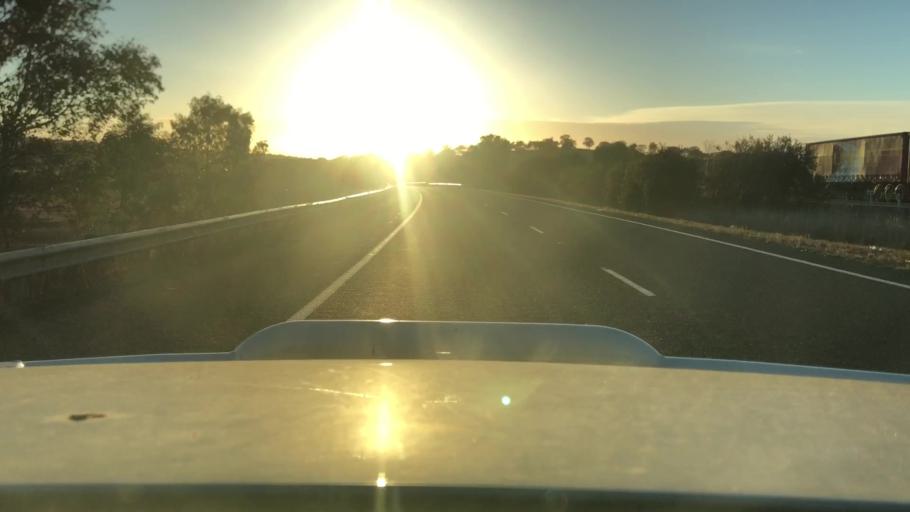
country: AU
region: New South Wales
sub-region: Goulburn Mulwaree
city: Goulburn
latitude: -34.7878
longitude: 149.6545
